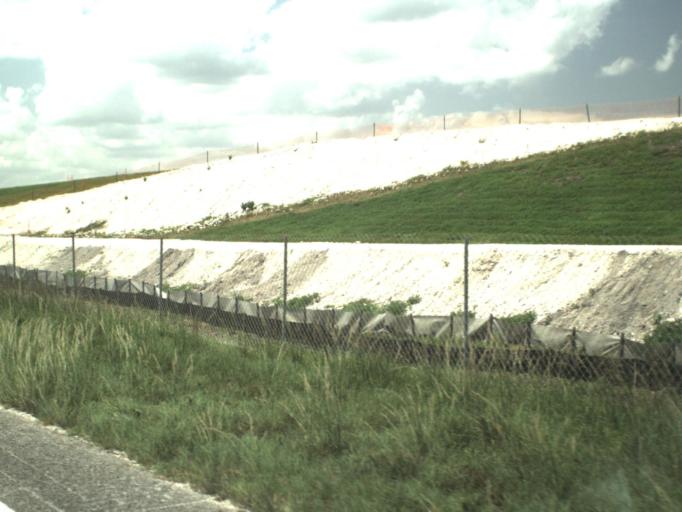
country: US
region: Florida
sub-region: Hendry County
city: Clewiston
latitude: 26.7283
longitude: -80.8543
